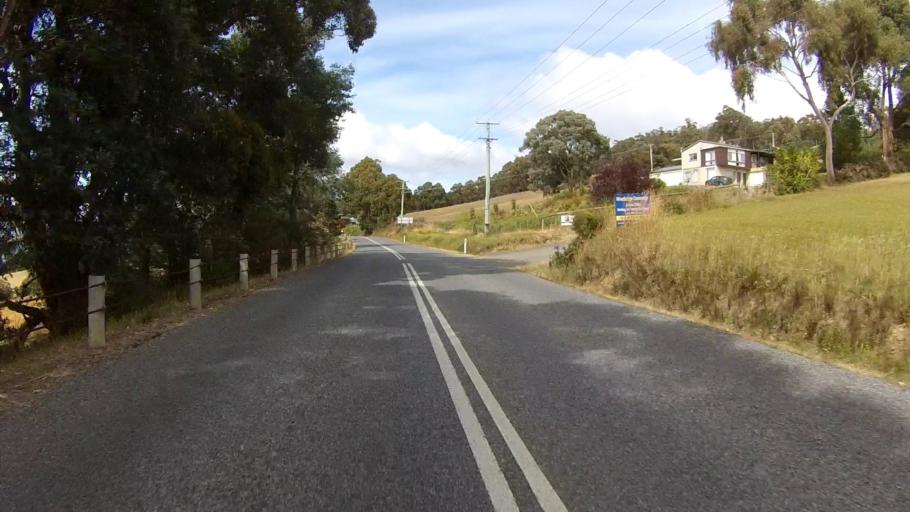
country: AU
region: Tasmania
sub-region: Kingborough
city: Kettering
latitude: -43.1399
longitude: 147.2440
